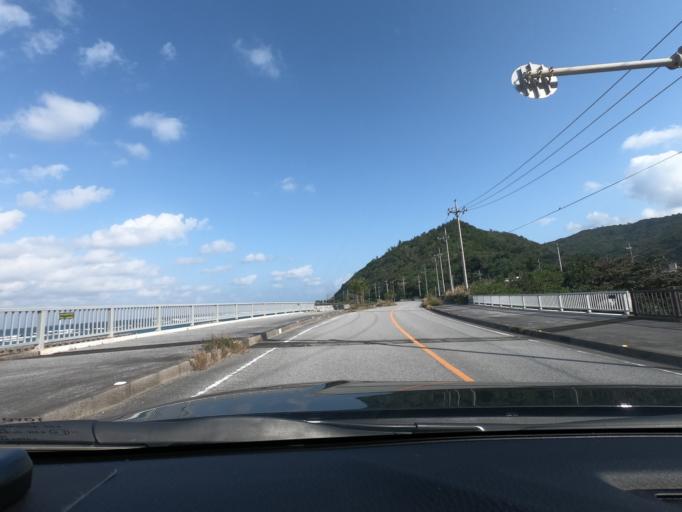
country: JP
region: Okinawa
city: Nago
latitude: 26.7561
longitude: 128.1883
